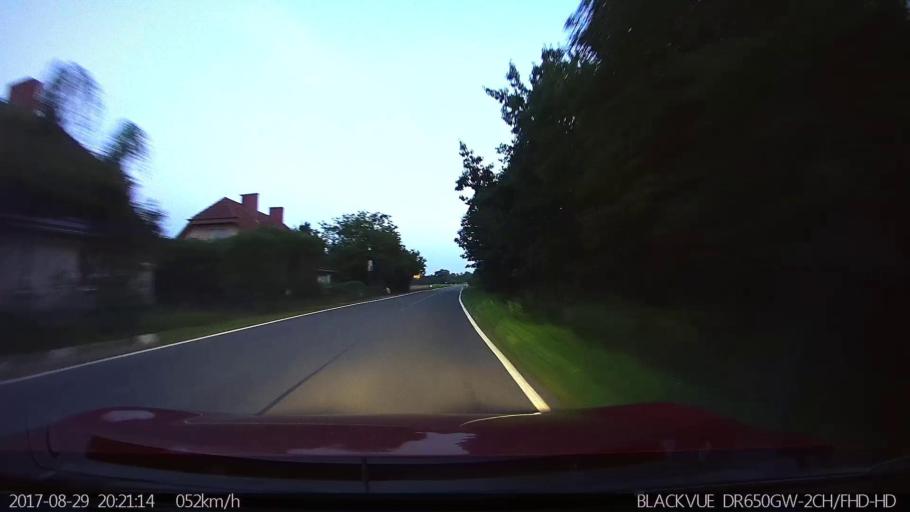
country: DE
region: Mecklenburg-Vorpommern
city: Velgast
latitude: 54.2510
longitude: 12.8243
